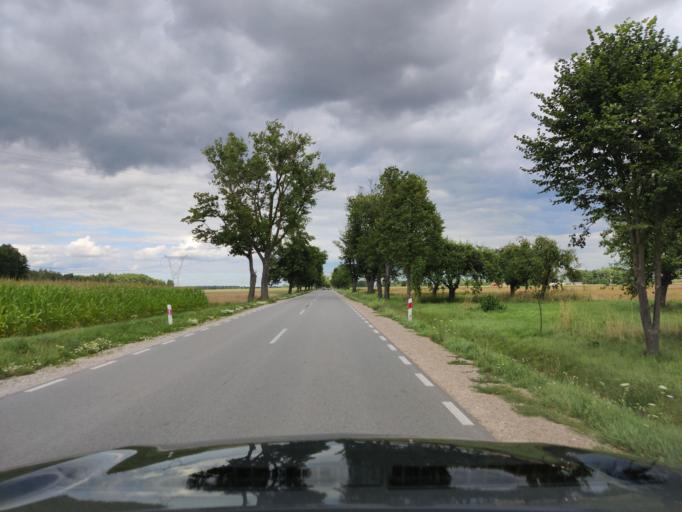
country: PL
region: Masovian Voivodeship
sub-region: Powiat sokolowski
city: Kosow Lacki
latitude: 52.6046
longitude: 22.1825
